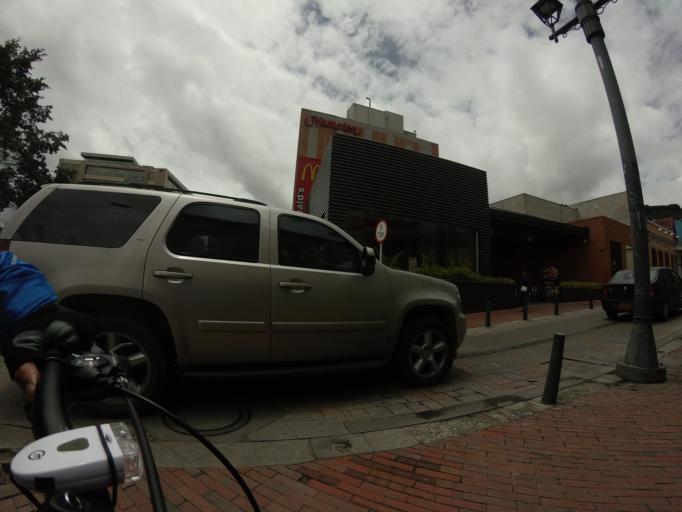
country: CO
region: Bogota D.C.
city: Barrio San Luis
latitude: 4.6953
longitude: -74.0322
